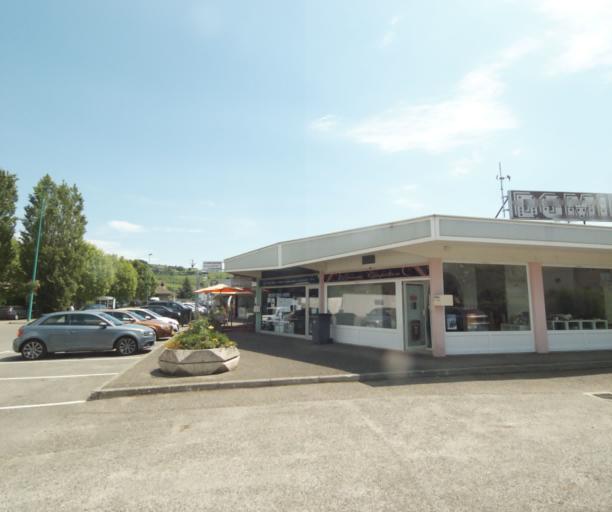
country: FR
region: Rhone-Alpes
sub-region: Departement de la Haute-Savoie
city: Douvaine
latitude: 46.3069
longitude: 6.3096
